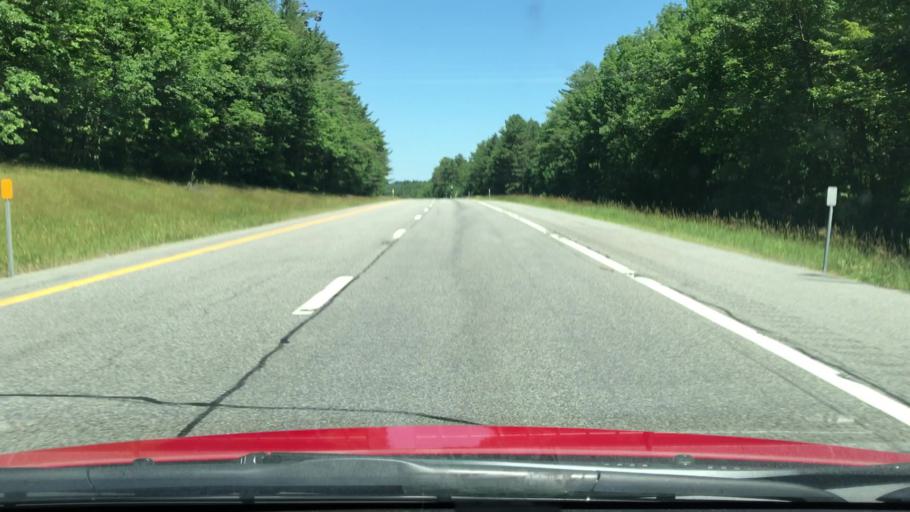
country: US
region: New York
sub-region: Essex County
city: Elizabethtown
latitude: 44.1525
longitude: -73.5827
